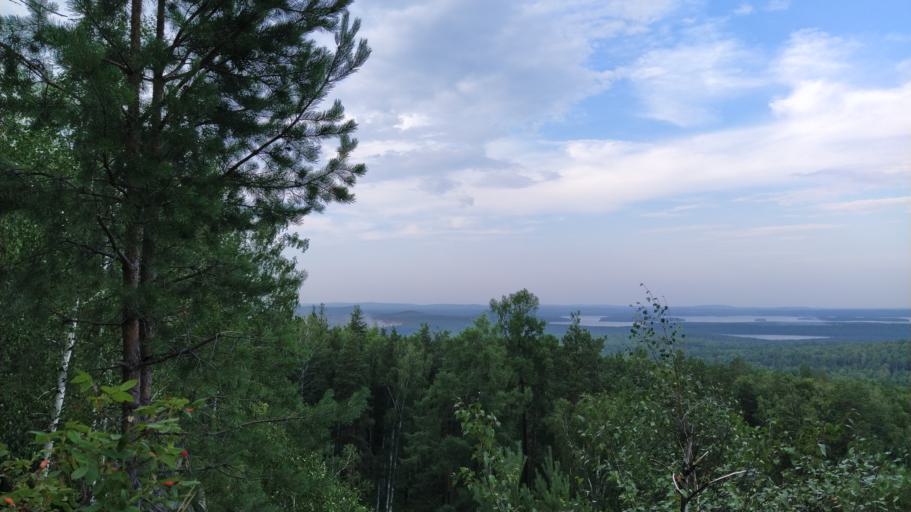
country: RU
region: Sverdlovsk
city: Revda
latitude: 56.7509
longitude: 60.0071
